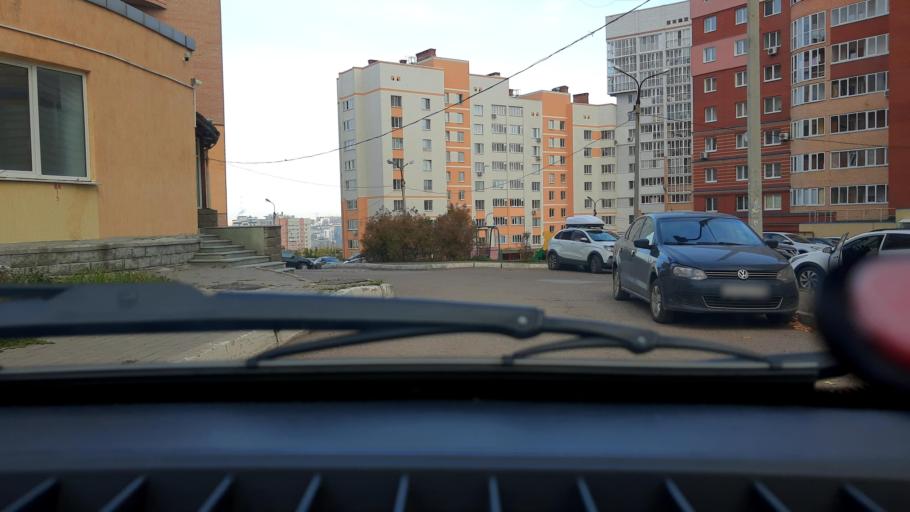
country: RU
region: Bashkortostan
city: Ufa
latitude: 54.7043
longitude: 55.9839
